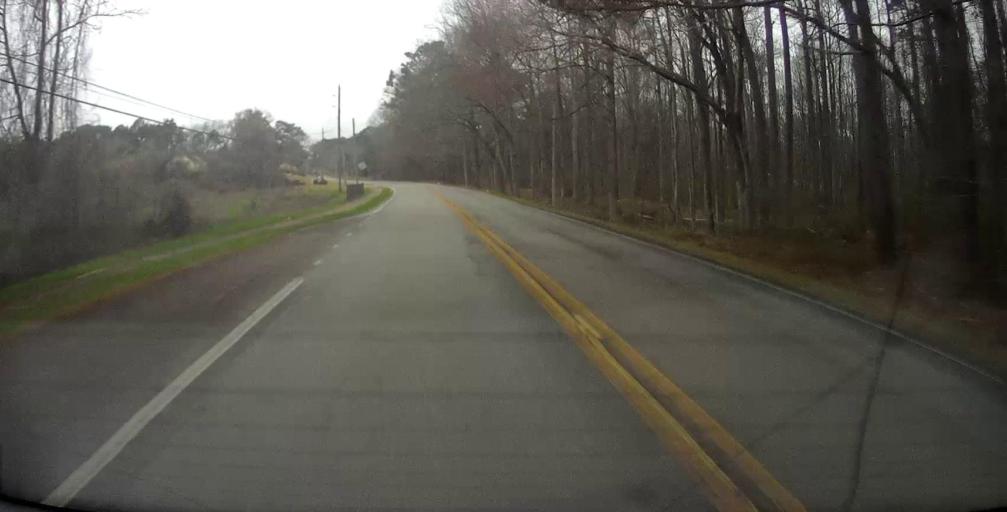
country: US
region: Georgia
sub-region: Lamar County
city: Barnesville
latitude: 33.0543
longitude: -84.1349
